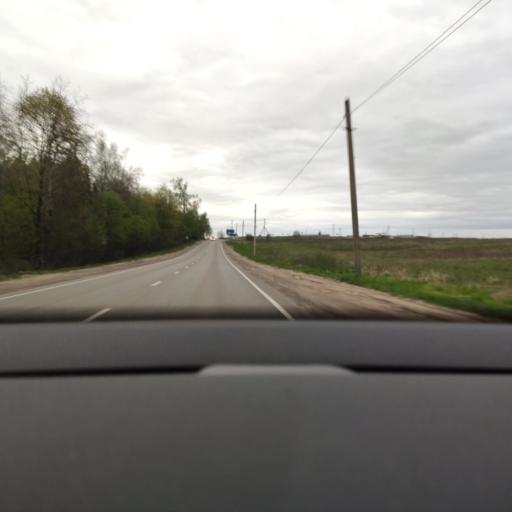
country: RU
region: Moskovskaya
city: Skhodnya
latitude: 55.9989
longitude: 37.3175
